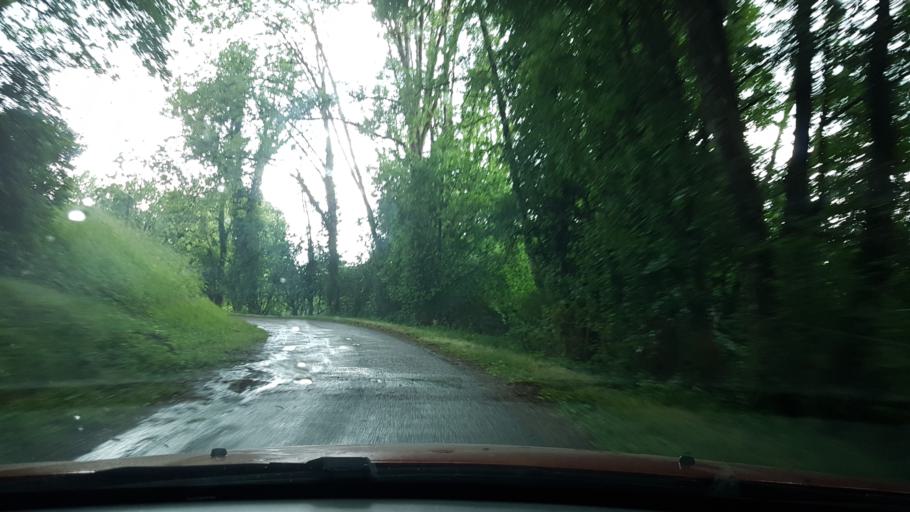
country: FR
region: Franche-Comte
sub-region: Departement du Jura
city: Clairvaux-les-Lacs
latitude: 46.5471
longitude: 5.6975
